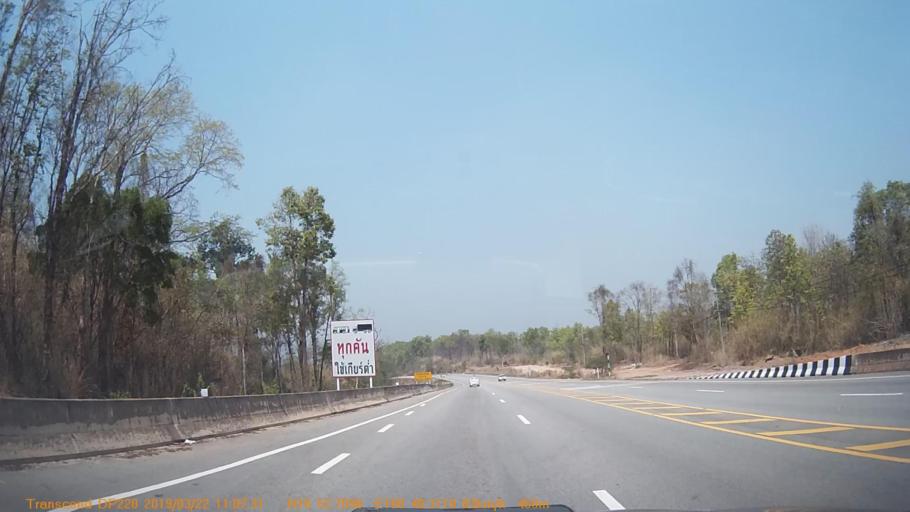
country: TH
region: Phitsanulok
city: Nakhon Thai
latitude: 16.8785
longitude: 100.8218
